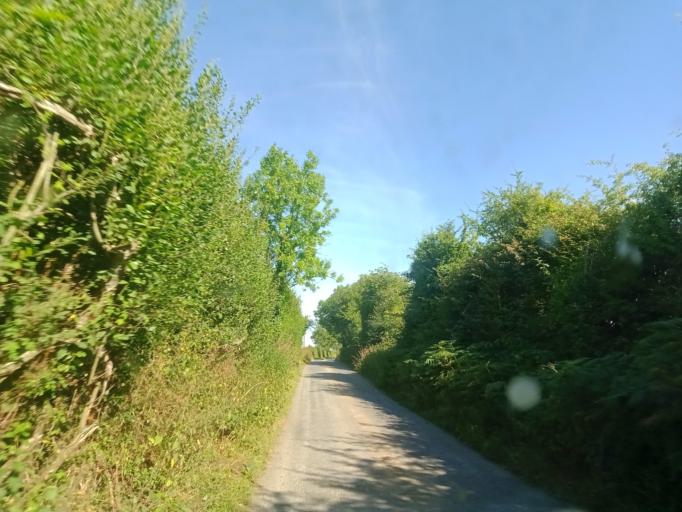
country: IE
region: Leinster
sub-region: Kilkenny
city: Ballyragget
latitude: 52.7899
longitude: -7.4230
